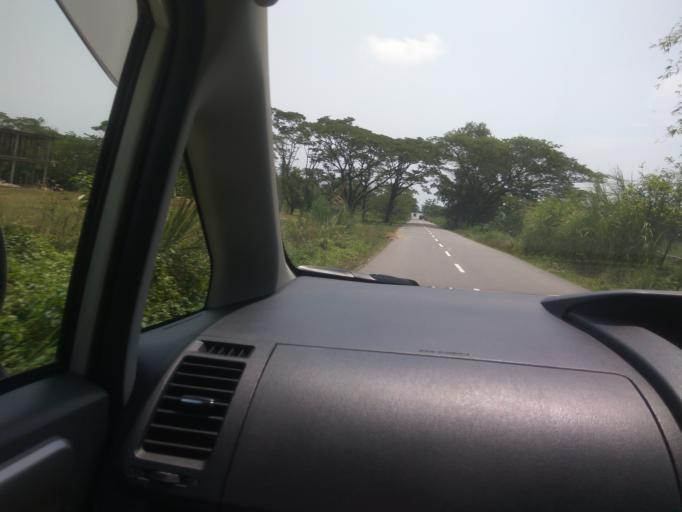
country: IN
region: Assam
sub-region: Karimganj
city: Karimganj
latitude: 24.9217
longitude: 92.1725
